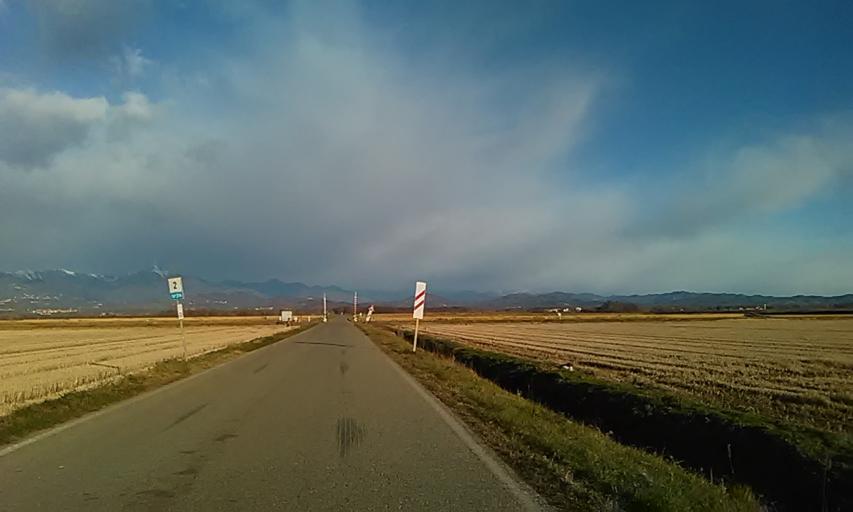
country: IT
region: Piedmont
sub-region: Provincia di Vercelli
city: Rovasenda
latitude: 45.5286
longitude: 8.2758
